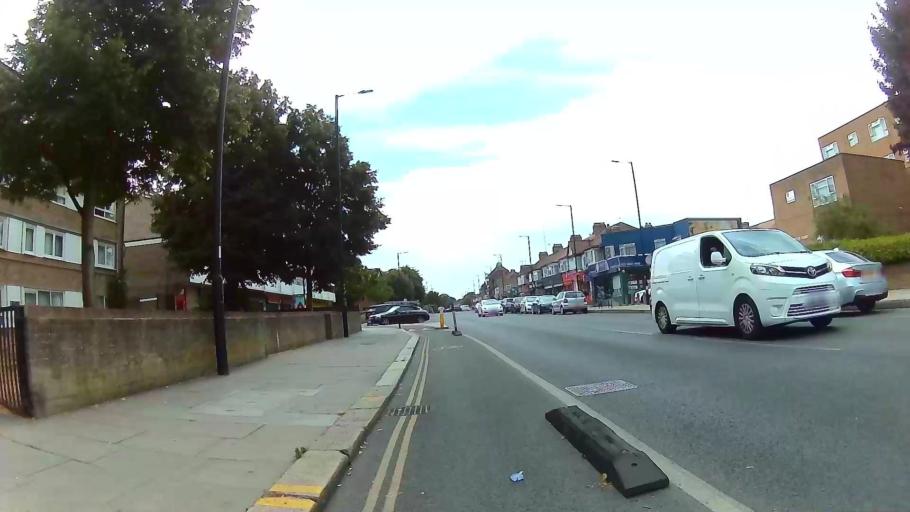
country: GB
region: England
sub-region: Greater London
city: Enfield
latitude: 51.6347
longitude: -0.0527
